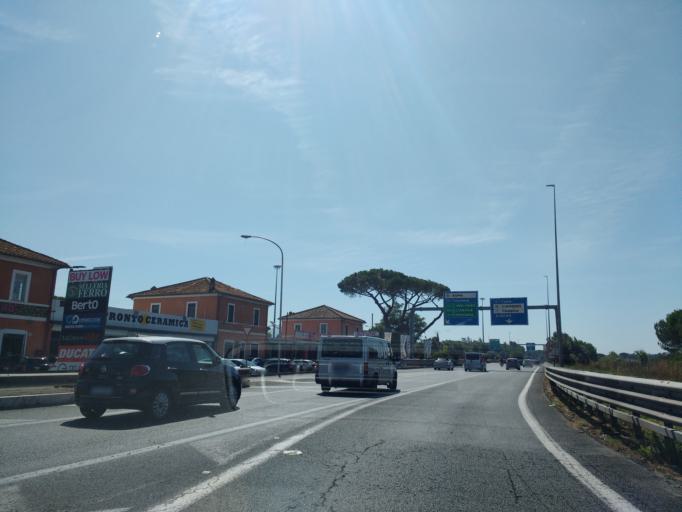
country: IT
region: Latium
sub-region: Citta metropolitana di Roma Capitale
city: Ciampino
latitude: 41.8116
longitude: 12.5734
